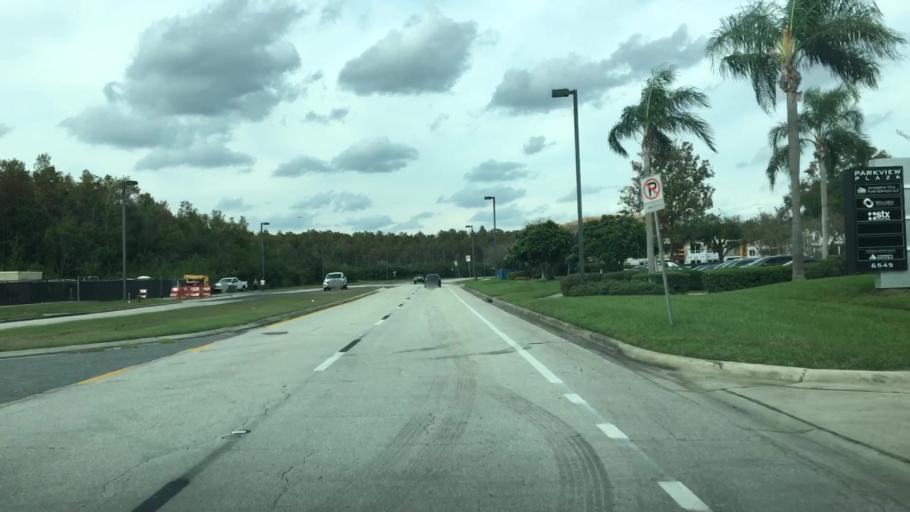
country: US
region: Florida
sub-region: Orange County
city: Conway
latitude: 28.4678
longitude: -81.2974
